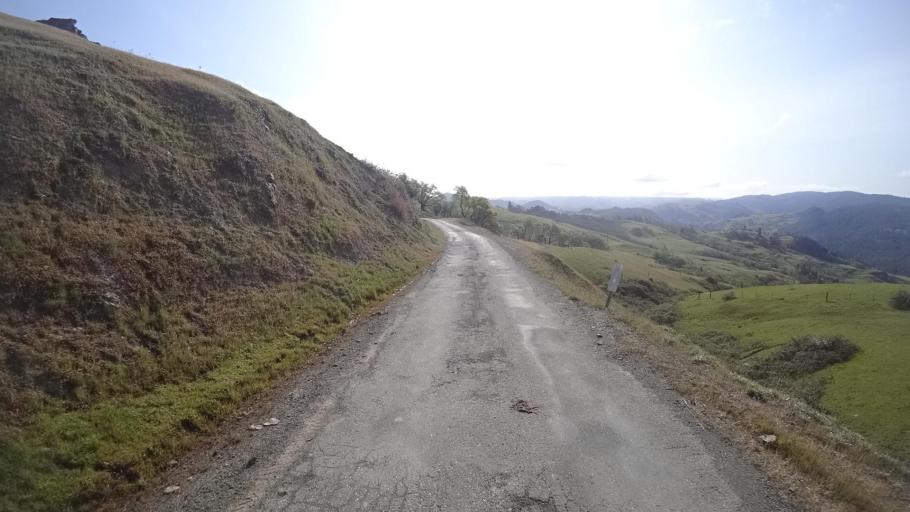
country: US
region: California
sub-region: Humboldt County
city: Hydesville
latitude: 40.6384
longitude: -123.8974
